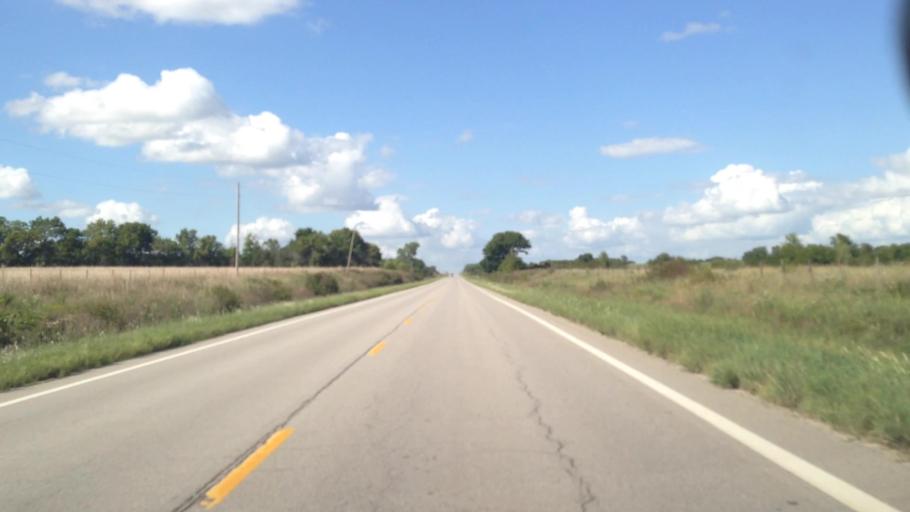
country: US
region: Kansas
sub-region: Neosho County
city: Erie
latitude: 37.7096
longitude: -95.1607
